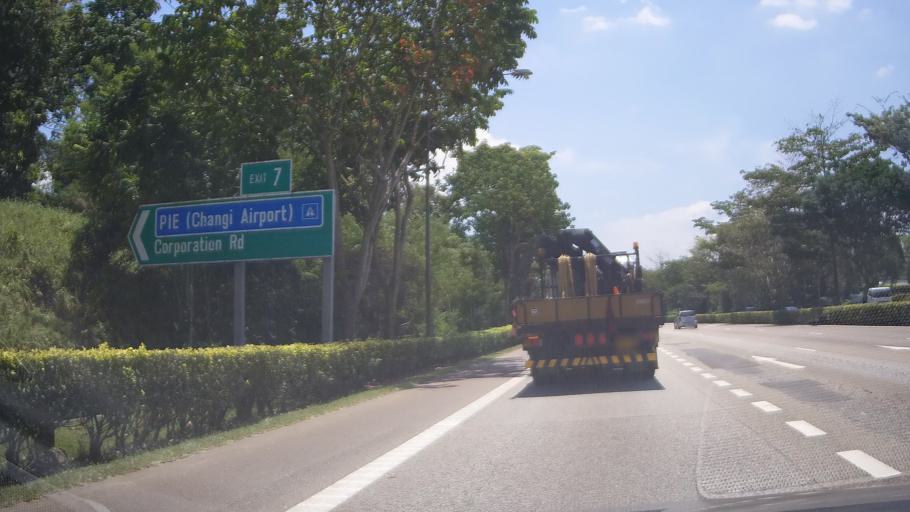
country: MY
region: Johor
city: Johor Bahru
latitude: 1.3671
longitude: 103.7114
